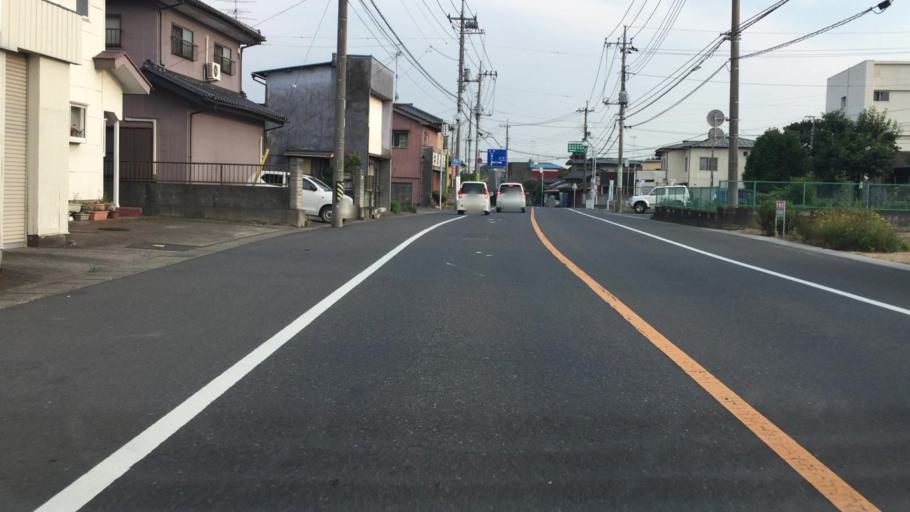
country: JP
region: Tochigi
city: Fujioka
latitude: 36.2629
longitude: 139.6499
